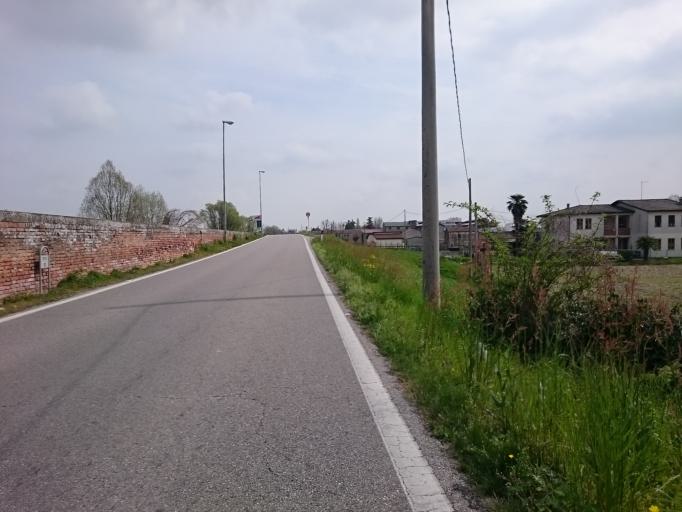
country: IT
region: Veneto
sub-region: Provincia di Padova
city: Bovolenta
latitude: 45.2669
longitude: 11.9462
